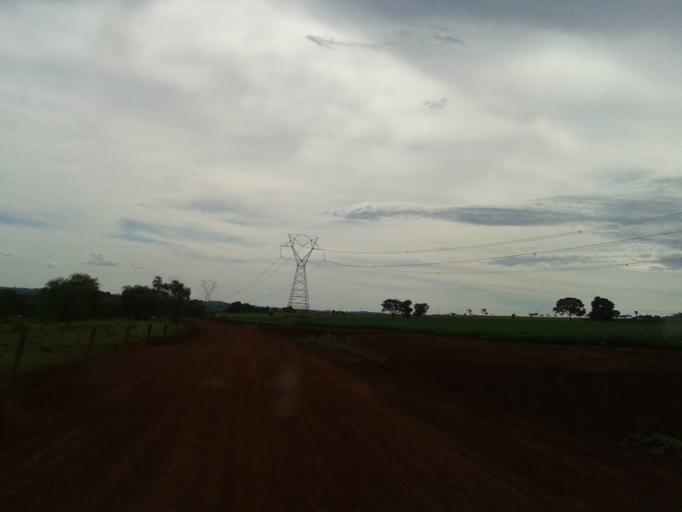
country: BR
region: Minas Gerais
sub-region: Centralina
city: Centralina
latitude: -18.6486
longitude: -49.3347
